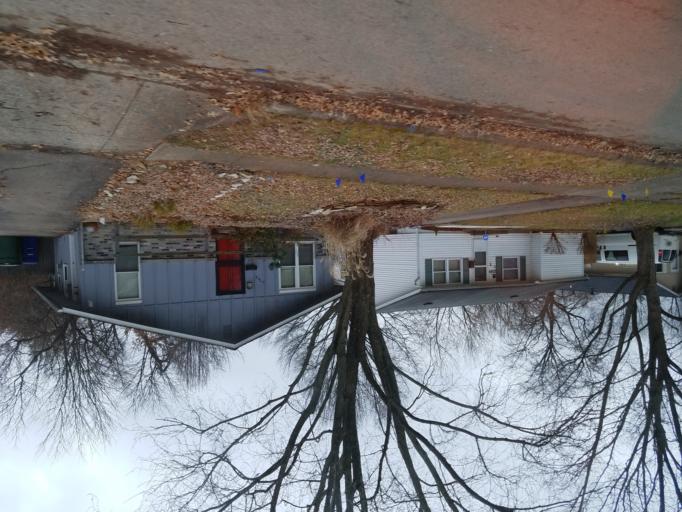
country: US
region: Ohio
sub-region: Franklin County
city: Minerva Park
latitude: 40.0919
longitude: -82.9556
